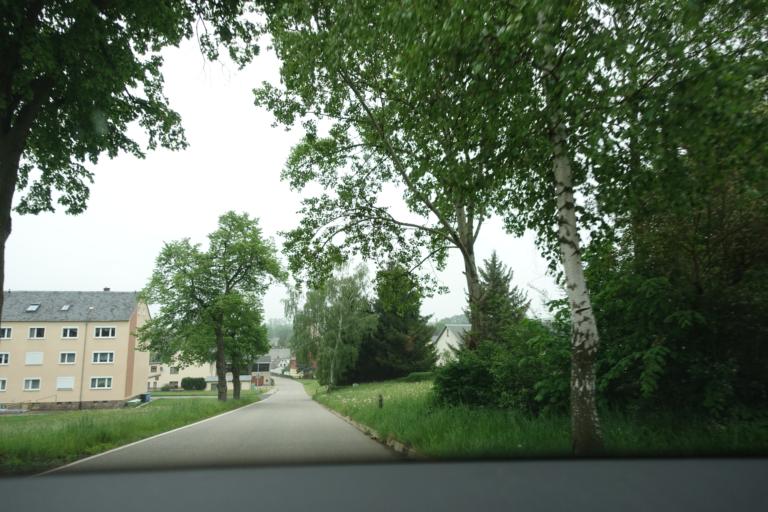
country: DE
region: Saxony
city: Eppendorf
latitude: 50.7827
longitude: 13.2662
